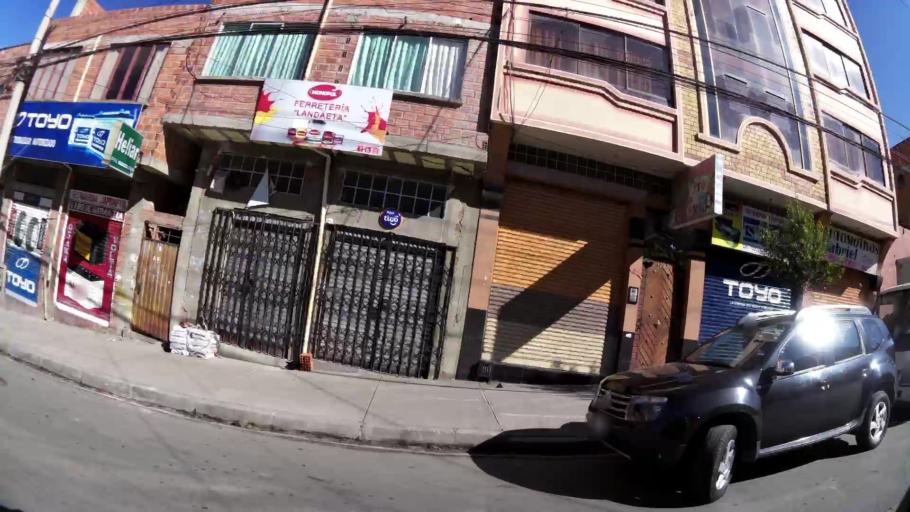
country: BO
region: La Paz
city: La Paz
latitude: -16.5117
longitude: -68.1397
